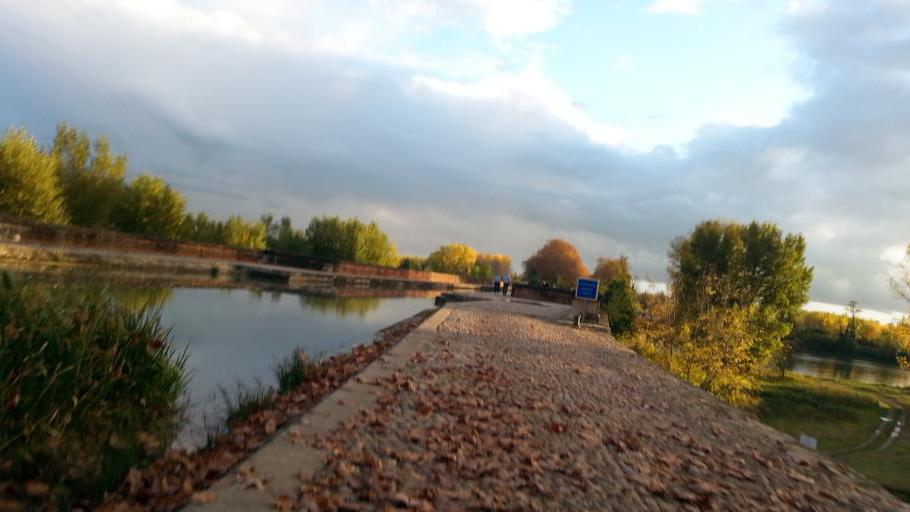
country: FR
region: Midi-Pyrenees
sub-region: Departement du Tarn-et-Garonne
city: Moissac
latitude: 44.0937
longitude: 1.1029
